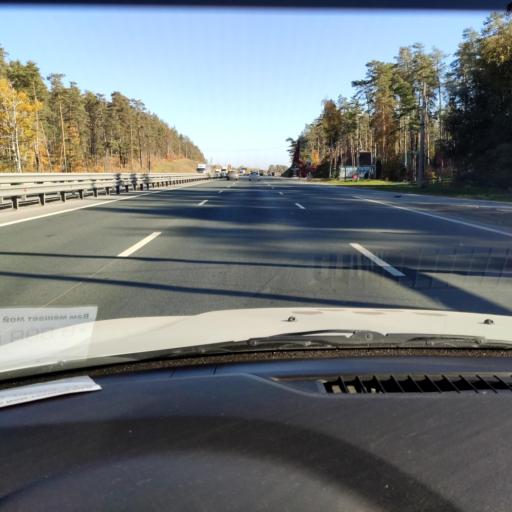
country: RU
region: Samara
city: Zhigulevsk
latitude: 53.5065
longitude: 49.5554
